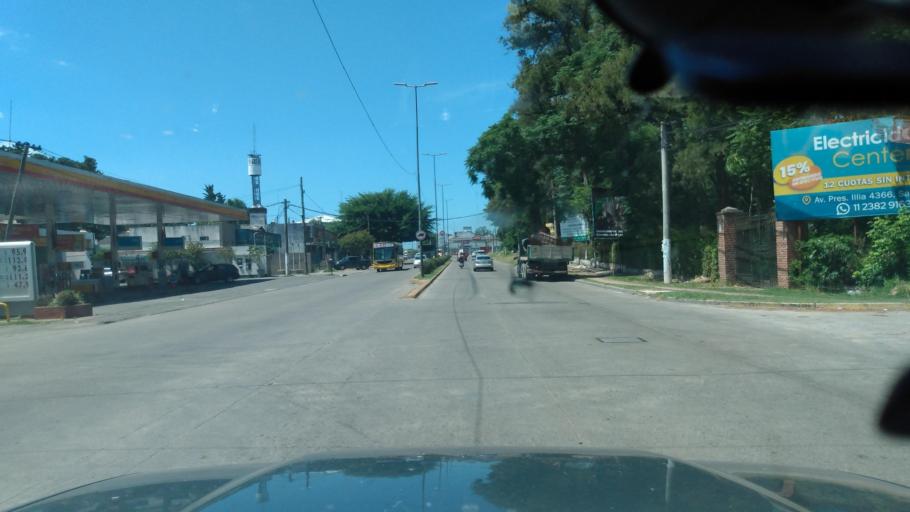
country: AR
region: Buenos Aires
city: Hurlingham
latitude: -34.5528
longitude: -58.7231
